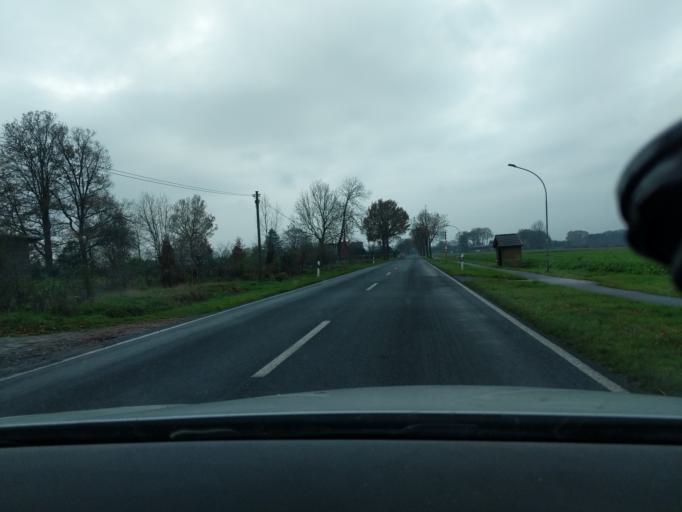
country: DE
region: Lower Saxony
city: Ahlerstedt
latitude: 53.3863
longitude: 9.4766
